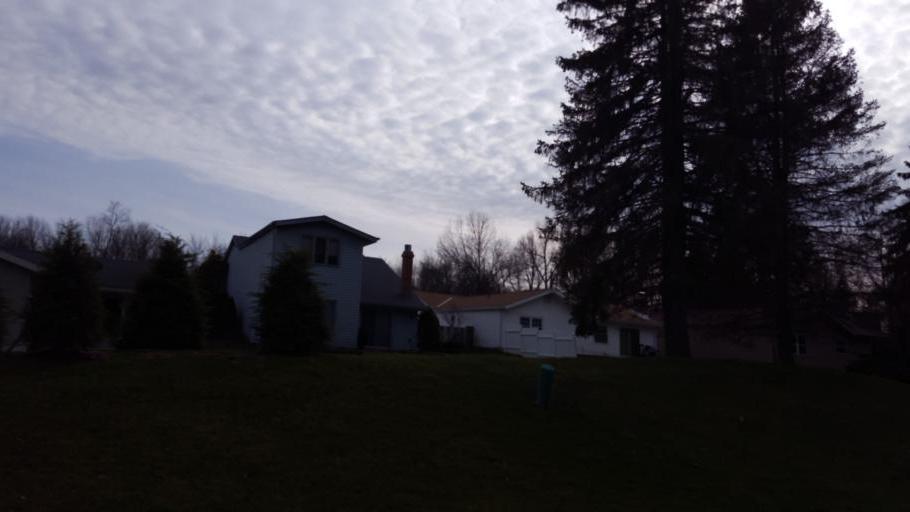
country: US
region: Ohio
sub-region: Richland County
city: Mansfield
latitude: 40.7107
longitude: -82.5282
